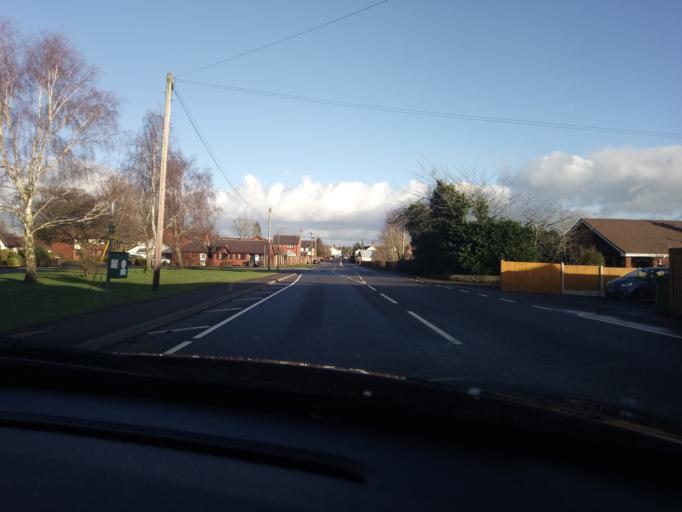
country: GB
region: Wales
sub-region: Wrexham
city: Overton
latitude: 52.9246
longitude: -2.9404
